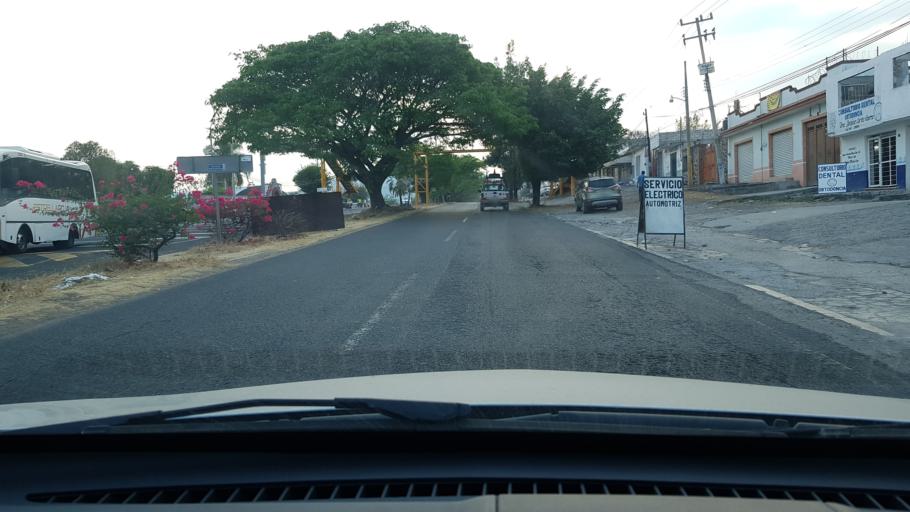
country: MX
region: Morelos
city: Yautepec
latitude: 18.8701
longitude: -99.0806
